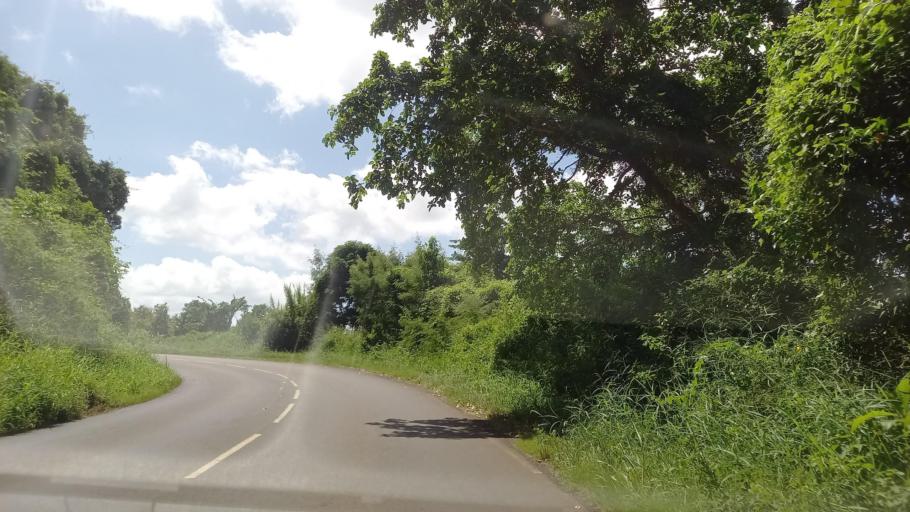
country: YT
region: Bandraboua
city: Bandraboua
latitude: -12.7188
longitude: 45.1291
